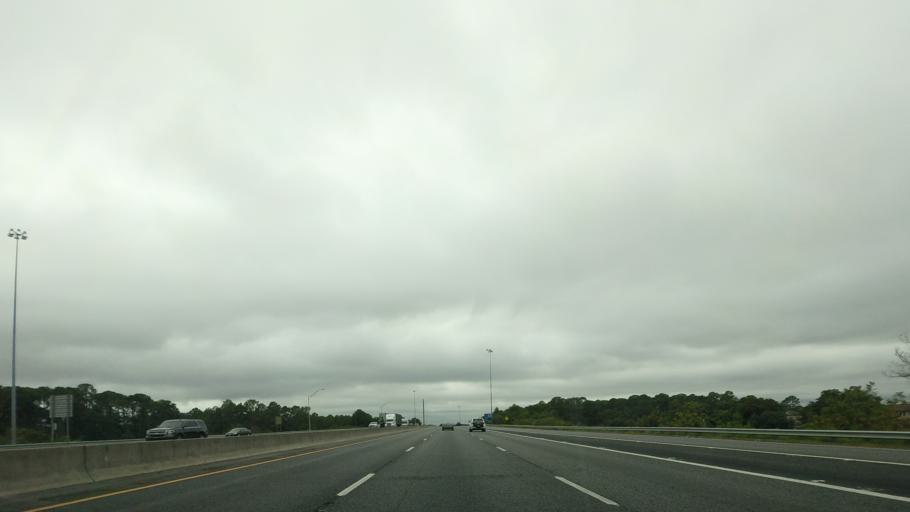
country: US
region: Georgia
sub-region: Tift County
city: Tifton
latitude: 31.4767
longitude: -83.5217
